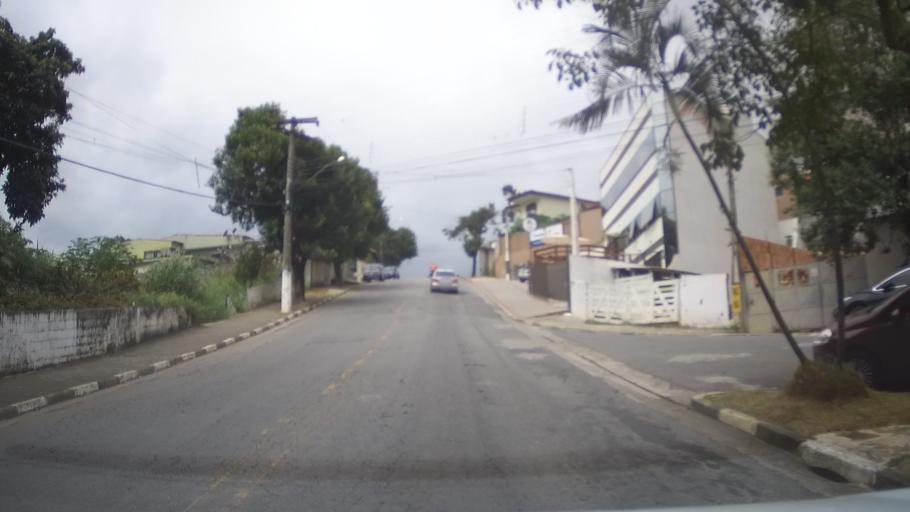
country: BR
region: Sao Paulo
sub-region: Aruja
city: Aruja
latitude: -23.3907
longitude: -46.3123
